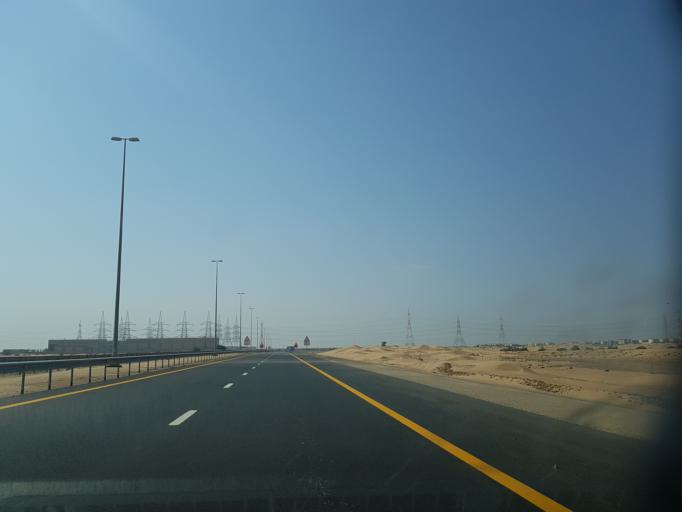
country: AE
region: Ash Shariqah
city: Sharjah
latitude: 25.2838
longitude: 55.5975
